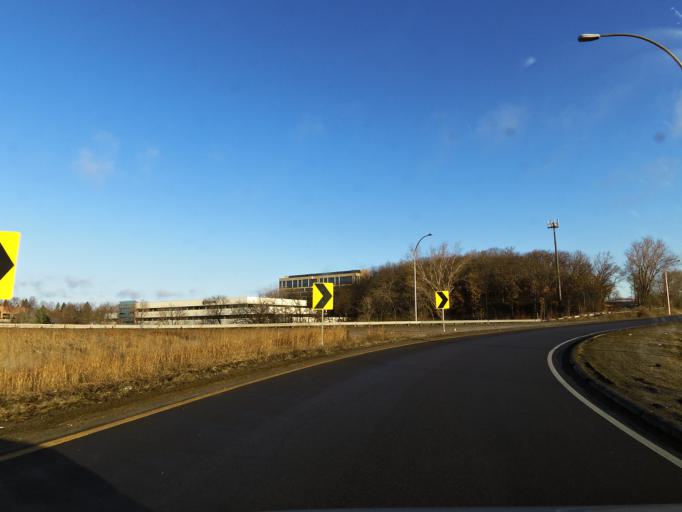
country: US
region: Minnesota
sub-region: Hennepin County
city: Edina
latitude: 44.8912
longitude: -93.4009
